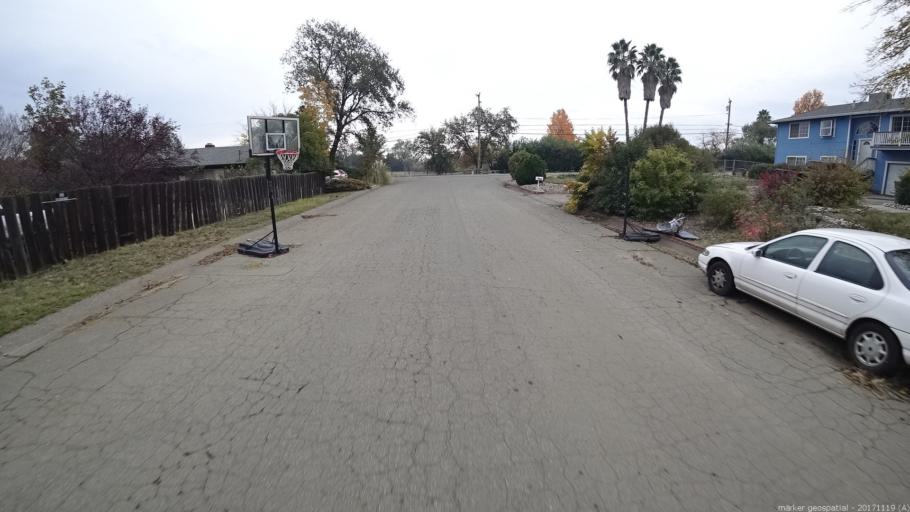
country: US
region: California
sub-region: Shasta County
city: Anderson
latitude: 40.4900
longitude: -122.3533
